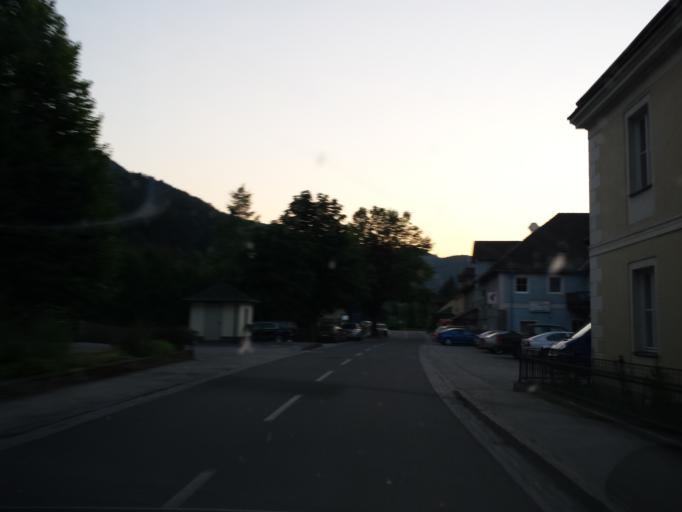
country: AT
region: Lower Austria
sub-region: Politischer Bezirk Lilienfeld
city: Ramsau
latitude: 48.0031
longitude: 15.8052
